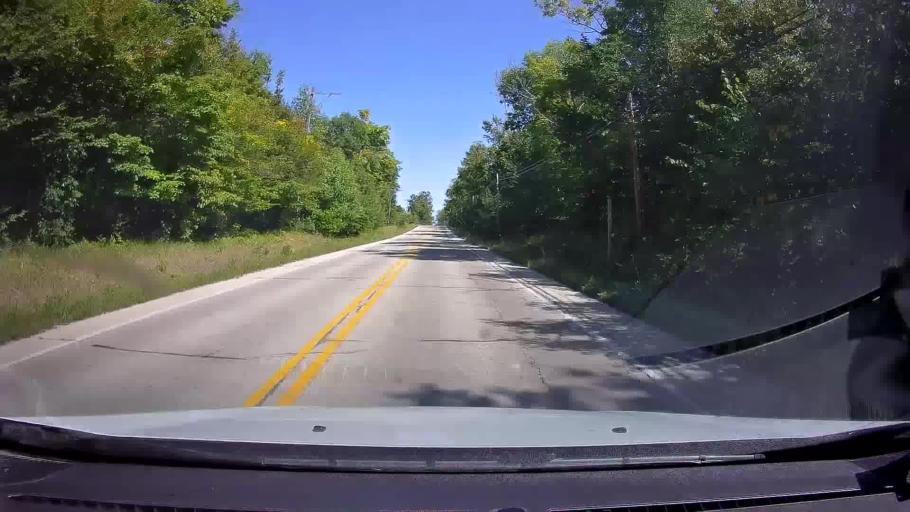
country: US
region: Michigan
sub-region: Delta County
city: Escanaba
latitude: 45.2595
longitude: -87.0374
